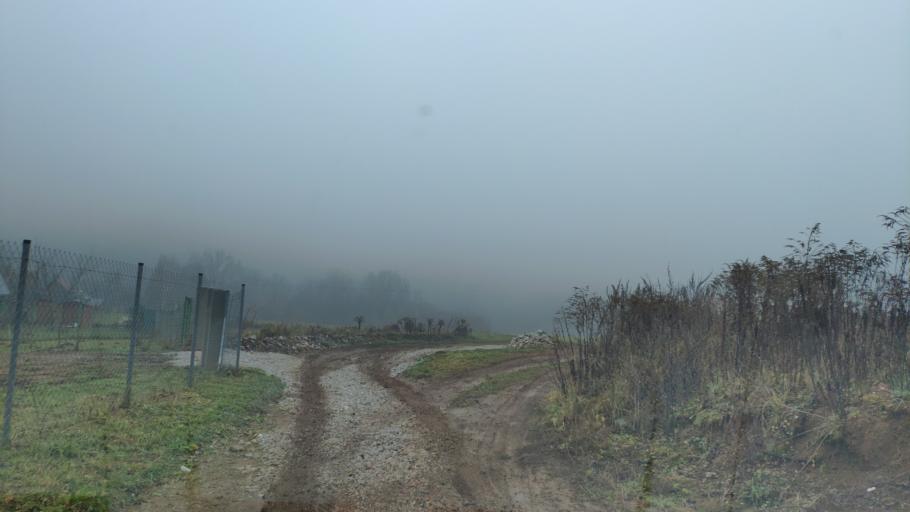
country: SK
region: Banskobystricky
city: Revuca
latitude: 48.6522
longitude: 20.2573
